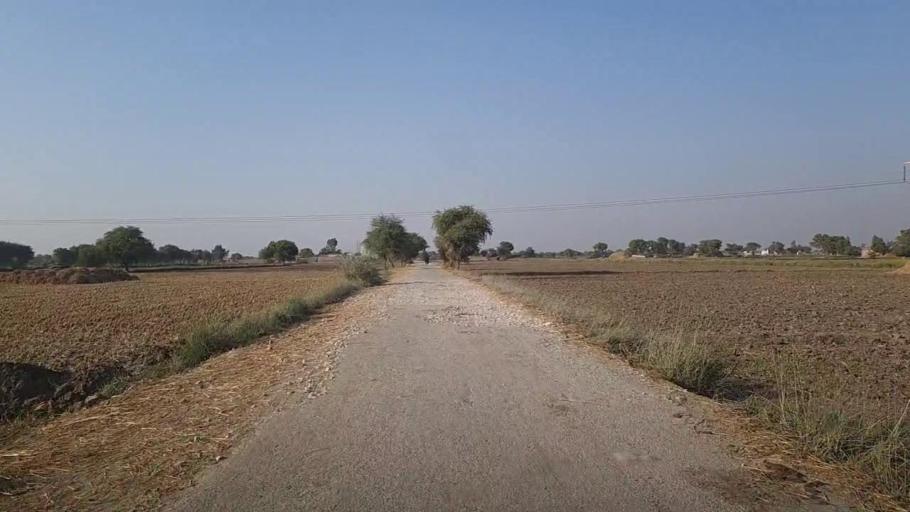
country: PK
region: Sindh
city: Kashmor
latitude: 28.4101
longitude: 69.4122
